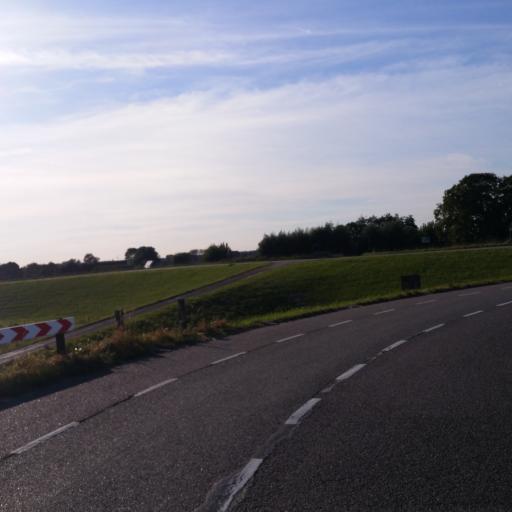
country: NL
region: Utrecht
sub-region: Gemeente Vianen
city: Vianen
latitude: 51.9996
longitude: 5.0682
